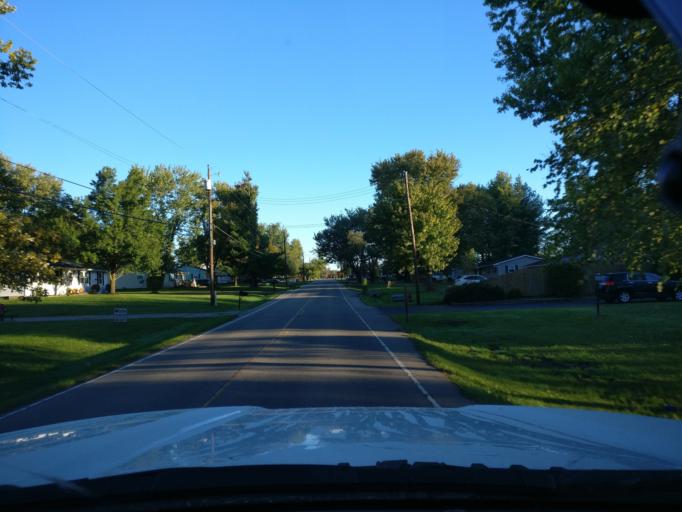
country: US
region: Ohio
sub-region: Warren County
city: Hunter
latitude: 39.5184
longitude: -84.2760
